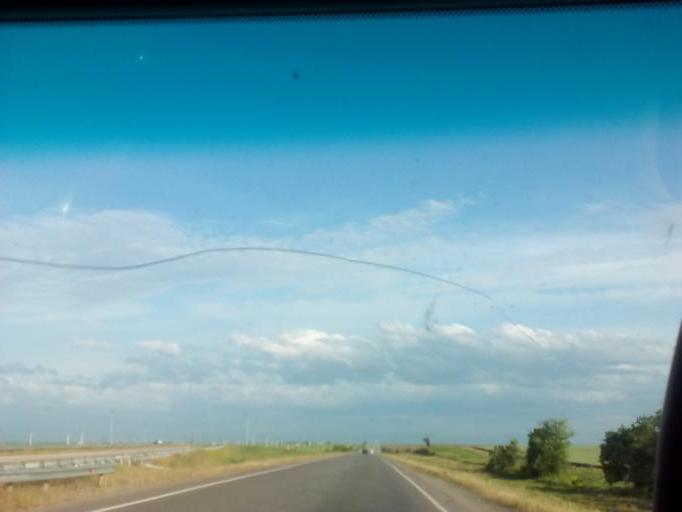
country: KZ
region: Ongtustik Qazaqstan
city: Temirlanovka
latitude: 42.5341
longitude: 69.3360
